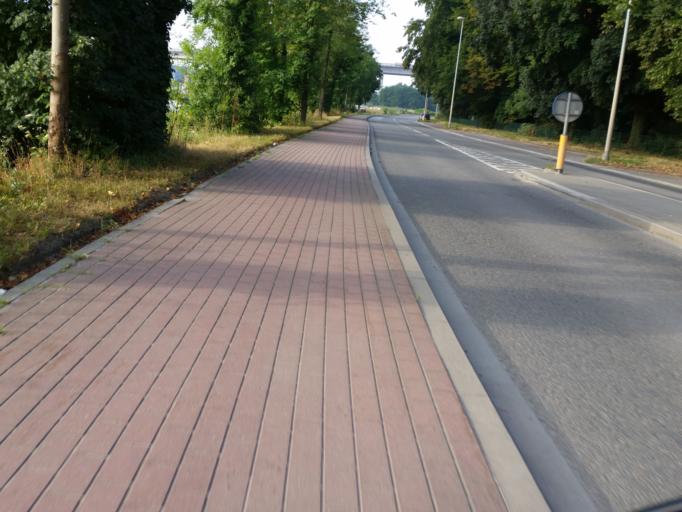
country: BE
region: Flanders
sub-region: Provincie Vlaams-Brabant
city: Vilvoorde
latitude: 50.9205
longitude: 4.4190
